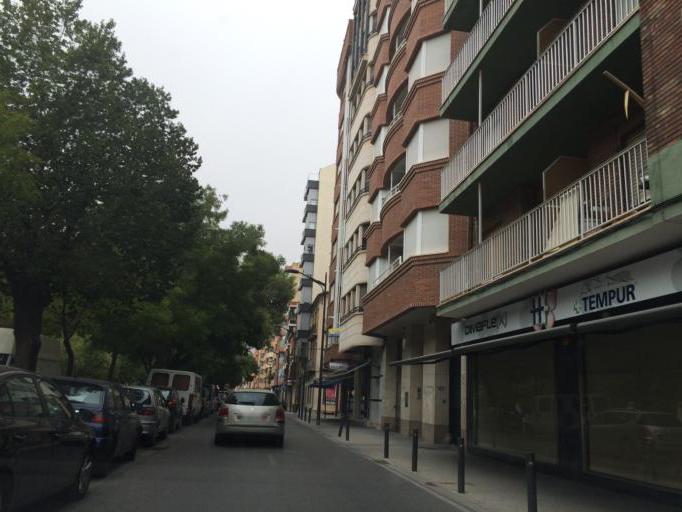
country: ES
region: Castille-La Mancha
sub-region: Provincia de Albacete
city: Albacete
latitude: 38.9972
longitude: -1.8645
